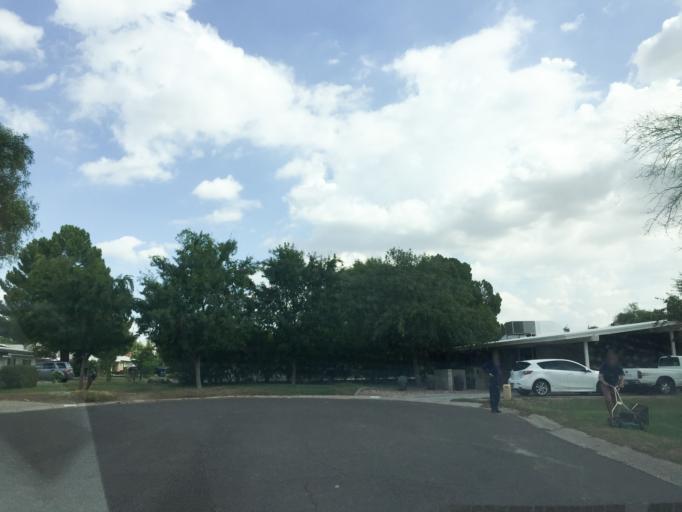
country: US
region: Arizona
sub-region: Maricopa County
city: Phoenix
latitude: 33.5324
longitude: -112.0535
